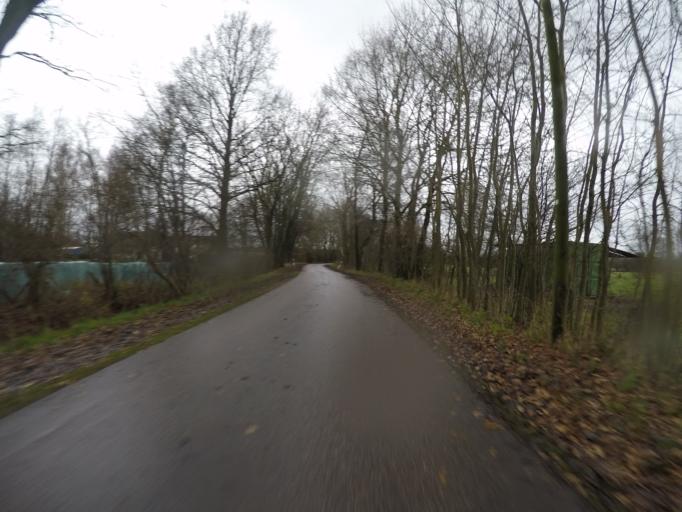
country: DE
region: Schleswig-Holstein
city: Bilsen
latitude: 53.7398
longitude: 9.8725
